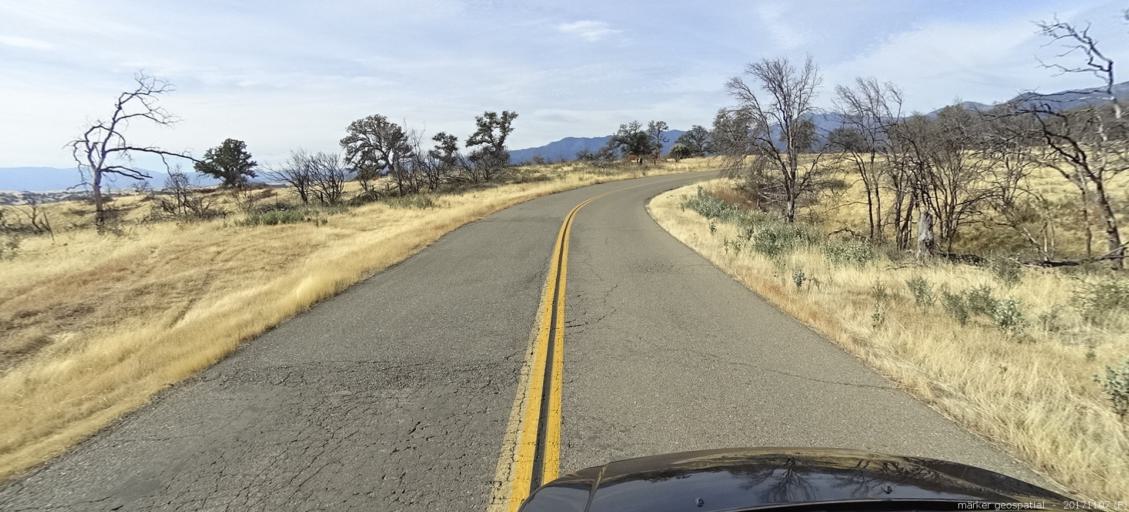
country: US
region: California
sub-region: Shasta County
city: Shasta
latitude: 40.4625
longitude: -122.5377
